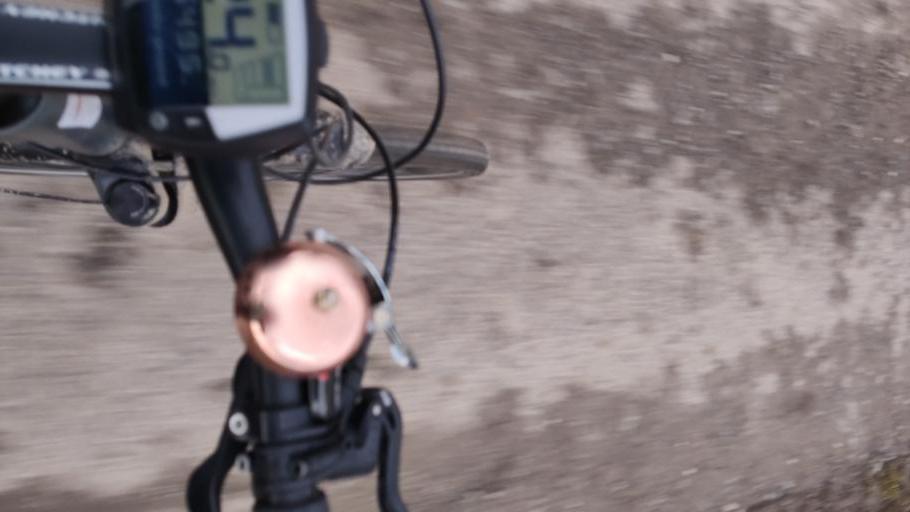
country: DE
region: Baden-Wuerttemberg
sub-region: Regierungsbezirk Stuttgart
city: Untergruppenbach
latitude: 49.0829
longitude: 9.2548
